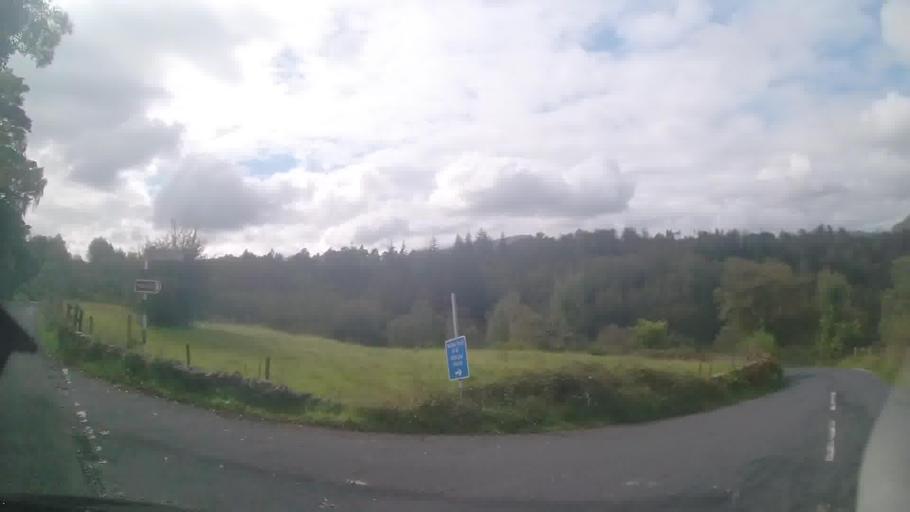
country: GB
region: England
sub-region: Cumbria
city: Ambleside
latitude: 54.4158
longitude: -3.0310
